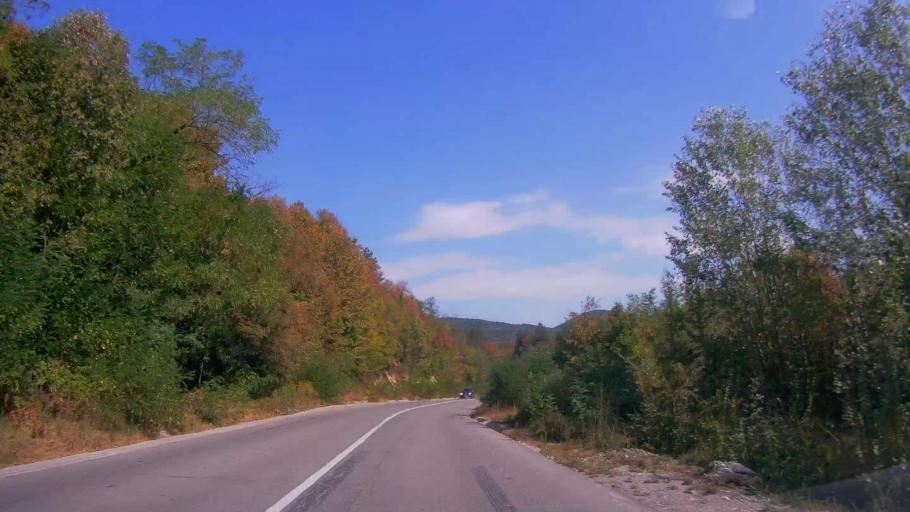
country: BG
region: Shumen
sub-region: Obshtina Smyadovo
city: Smyadovo
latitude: 43.0141
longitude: 27.0463
